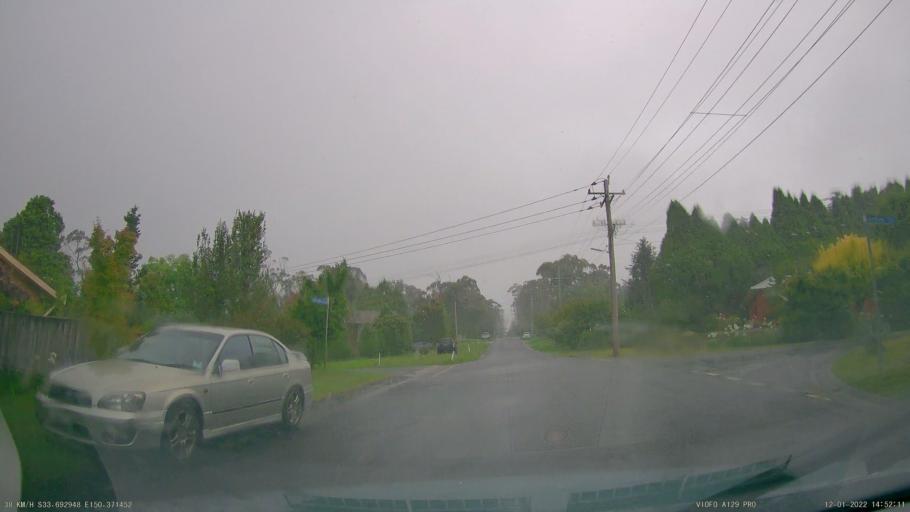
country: AU
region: New South Wales
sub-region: Blue Mountains Municipality
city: Leura
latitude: -33.6931
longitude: 150.3714
